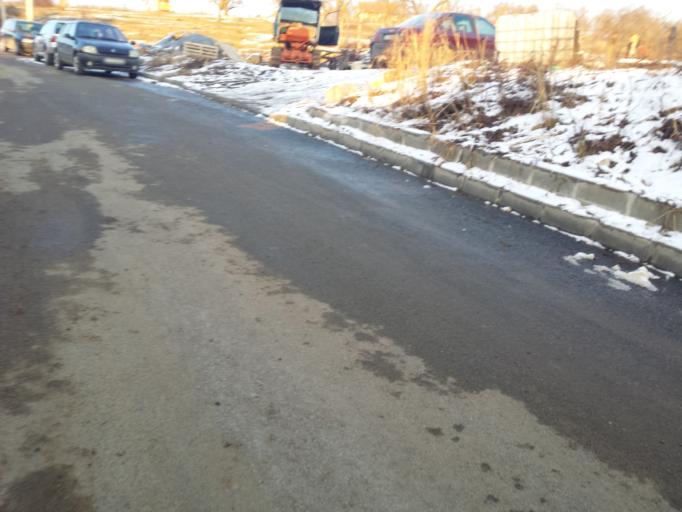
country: RO
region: Cluj
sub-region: Municipiul Cluj-Napoca
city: Cluj-Napoca
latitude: 46.7949
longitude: 23.5842
